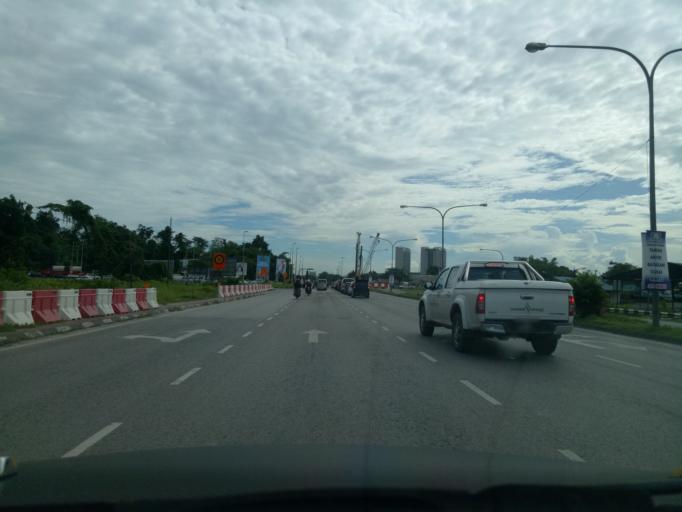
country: MY
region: Sarawak
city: Kuching
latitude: 1.4984
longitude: 110.3321
